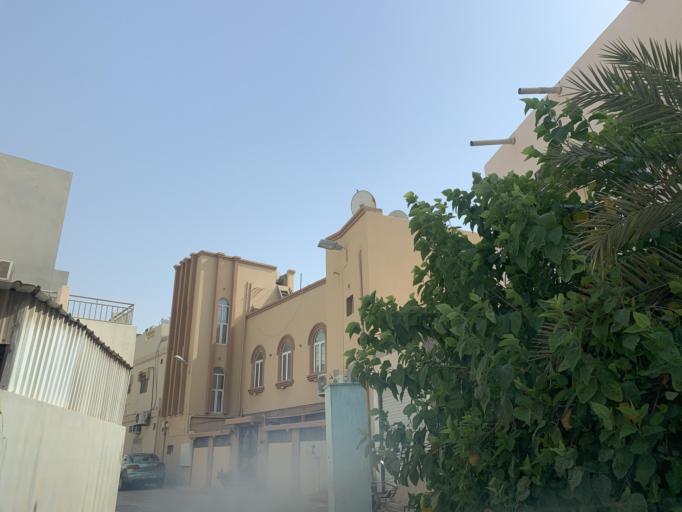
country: BH
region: Manama
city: Jidd Hafs
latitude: 26.2159
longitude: 50.5120
